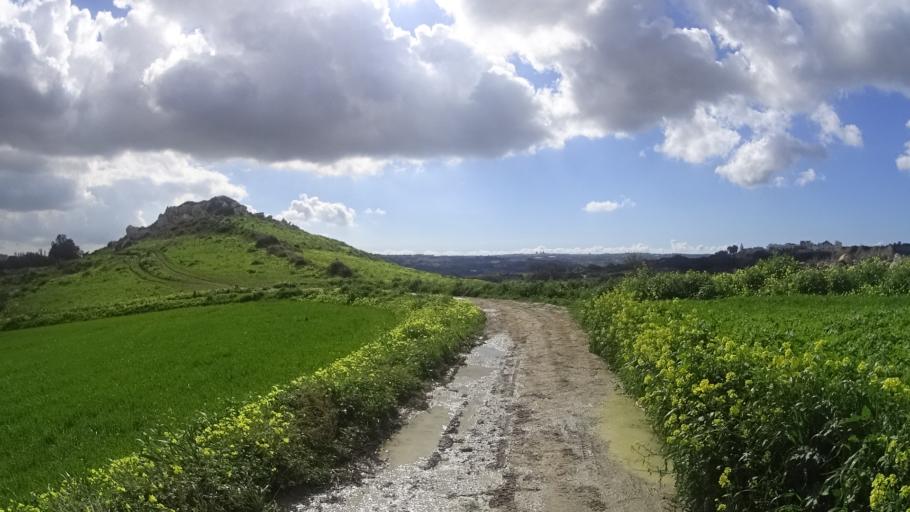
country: MT
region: L-Imtarfa
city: Imtarfa
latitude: 35.9004
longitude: 14.3844
